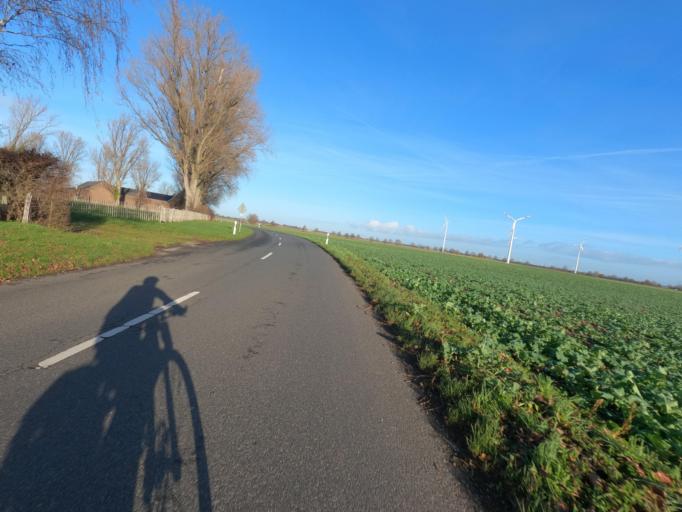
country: DE
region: North Rhine-Westphalia
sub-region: Regierungsbezirk Koln
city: Titz
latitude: 50.9611
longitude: 6.4118
